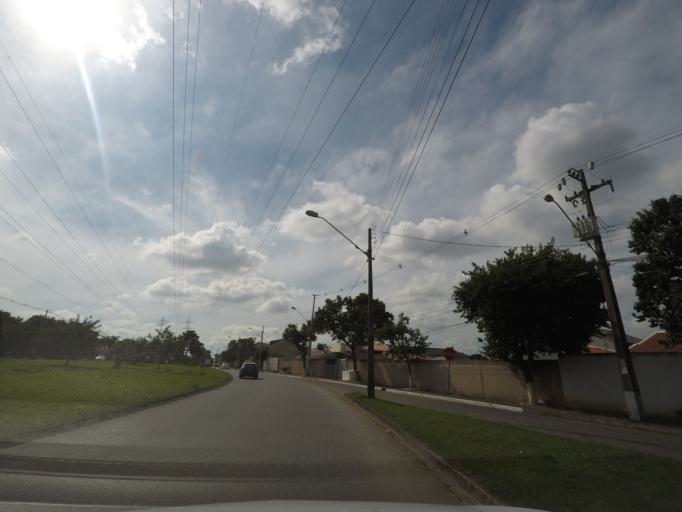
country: BR
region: Parana
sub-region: Sao Jose Dos Pinhais
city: Sao Jose dos Pinhais
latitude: -25.4899
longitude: -49.2066
